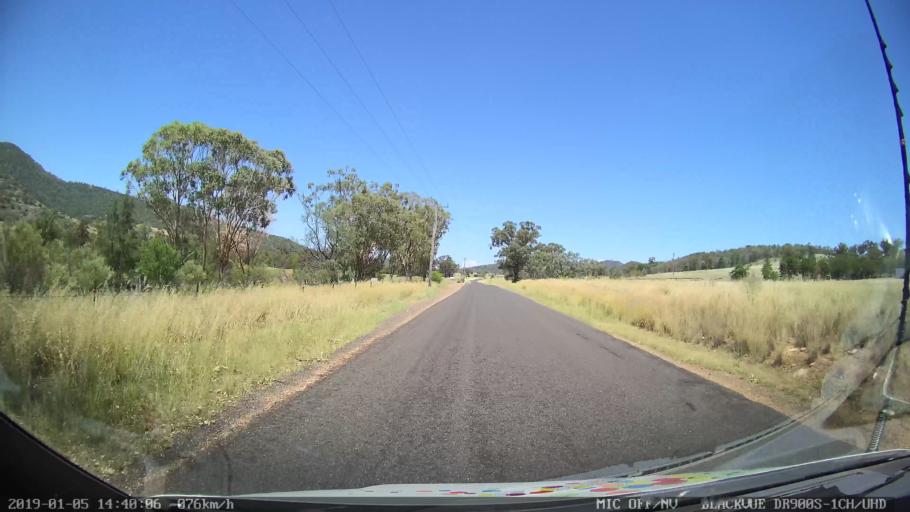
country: AU
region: New South Wales
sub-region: Tamworth Municipality
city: Phillip
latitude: -31.2574
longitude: 150.7087
